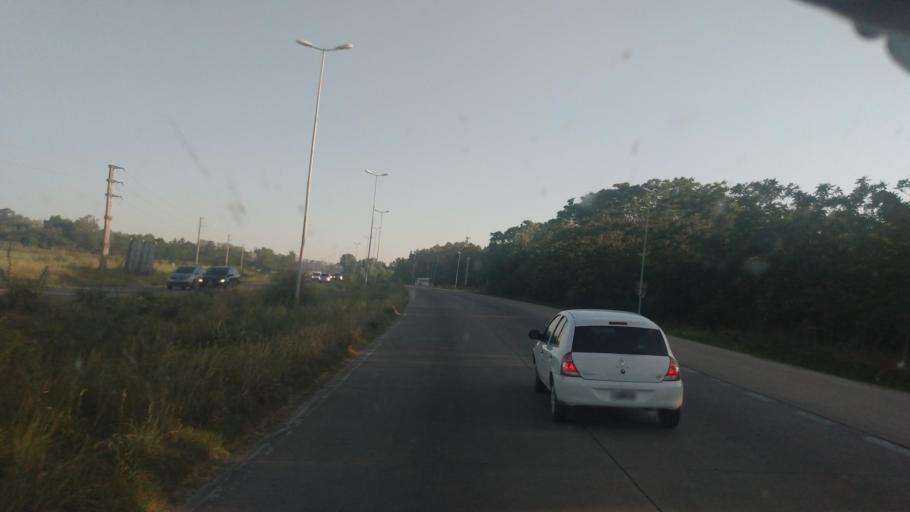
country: AR
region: Buenos Aires
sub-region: Partido de Campana
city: Campana
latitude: -34.2446
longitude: -58.9663
